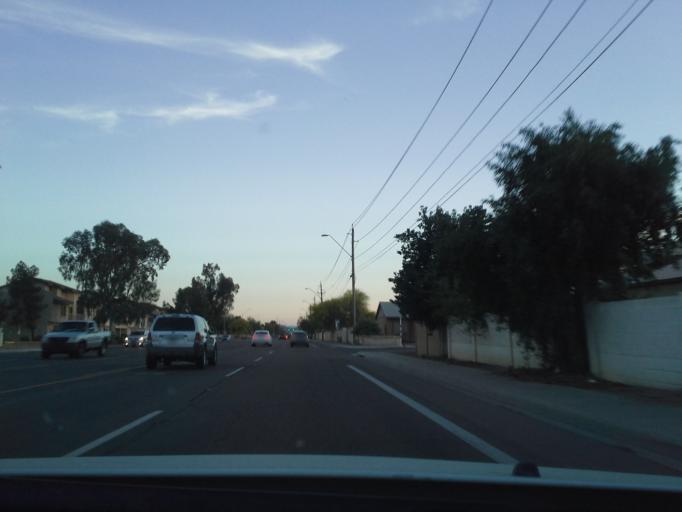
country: US
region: Arizona
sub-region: Maricopa County
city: Glendale
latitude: 33.6663
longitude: -112.0658
